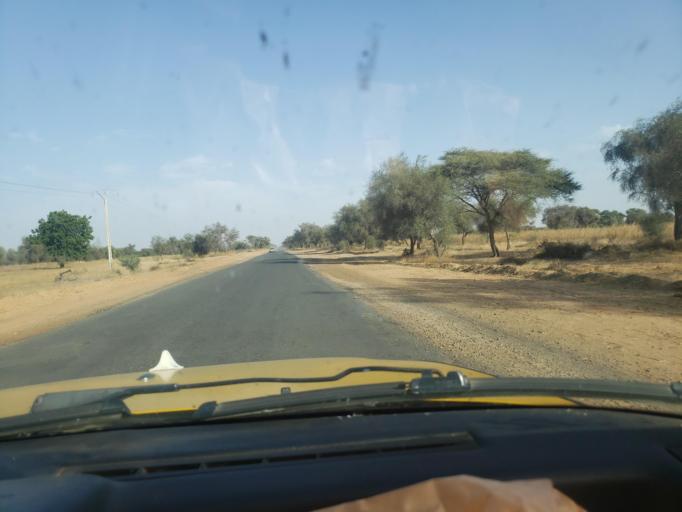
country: SN
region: Louga
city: Louga
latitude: 15.5060
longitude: -15.9624
